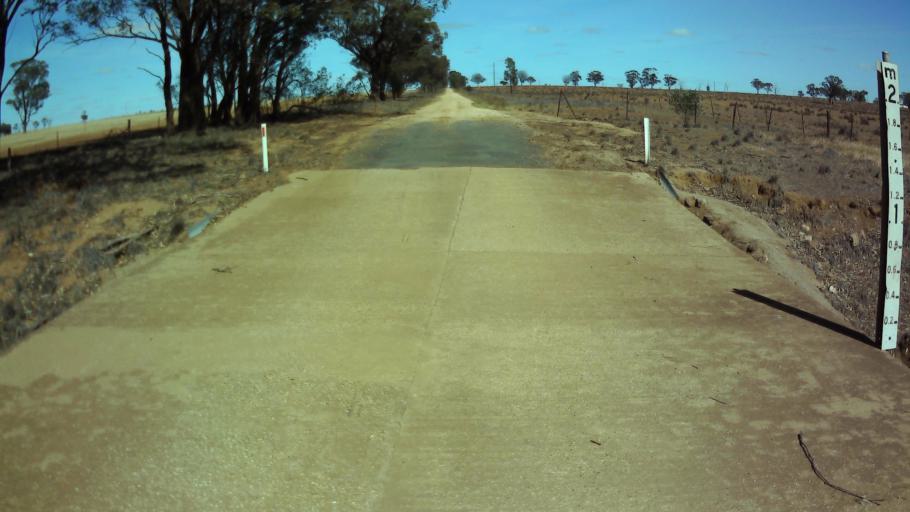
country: AU
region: New South Wales
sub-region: Weddin
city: Grenfell
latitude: -33.7282
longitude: 147.8900
